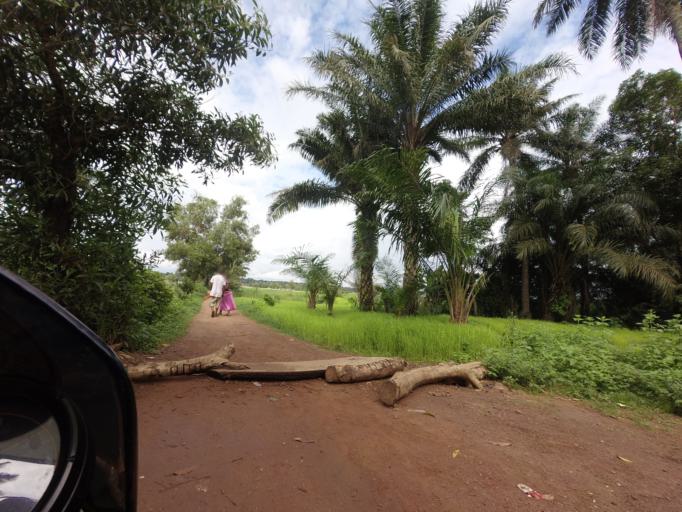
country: SL
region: Northern Province
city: Mambolo
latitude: 9.0046
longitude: -12.9643
